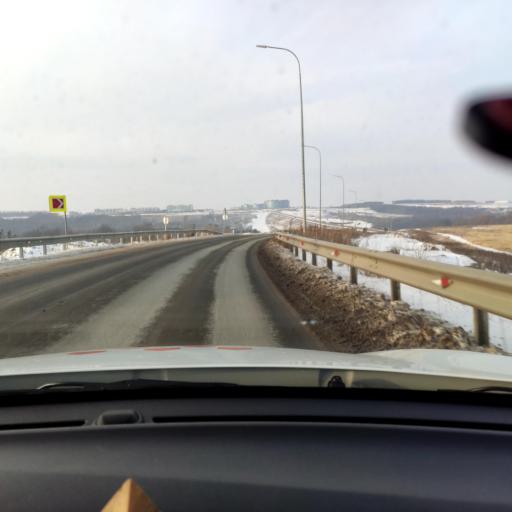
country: RU
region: Tatarstan
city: Sviyazhsk
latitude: 55.7403
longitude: 48.7792
